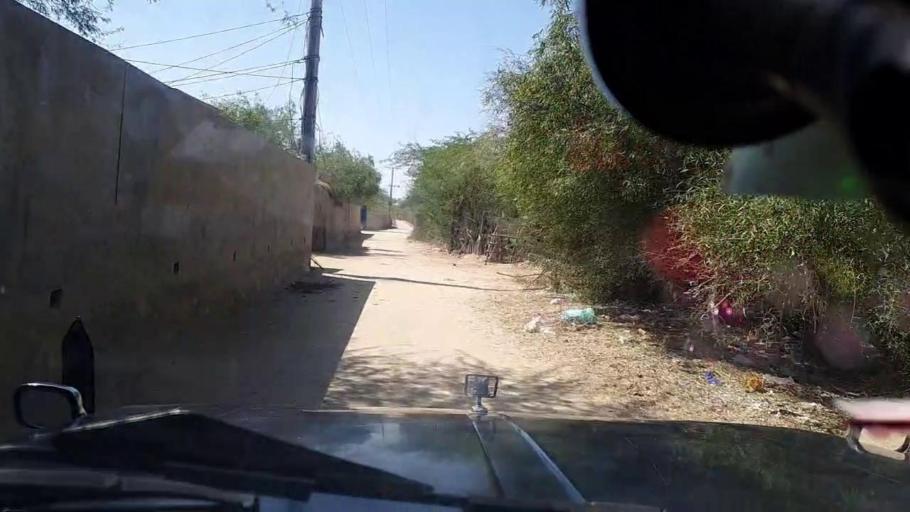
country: PK
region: Sindh
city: Mithi
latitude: 24.5955
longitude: 69.7088
